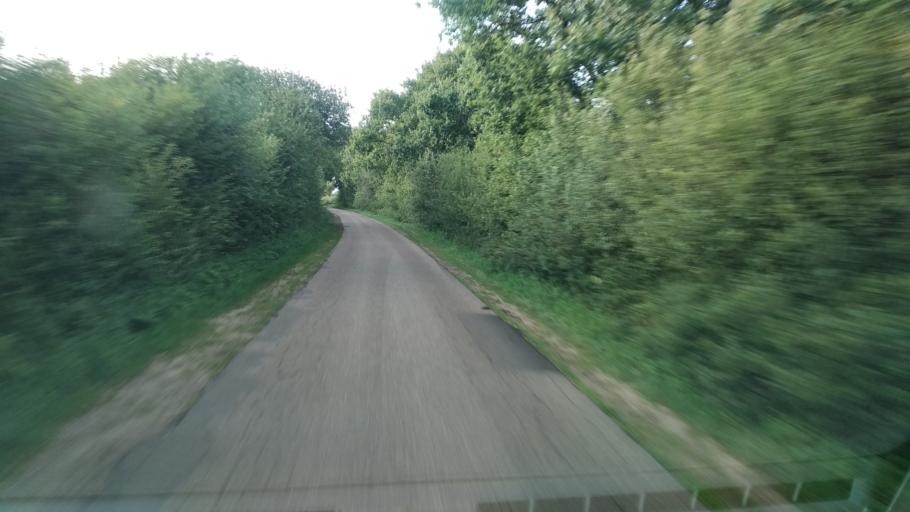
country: DE
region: Schleswig-Holstein
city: Klein Bennebek
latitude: 54.4081
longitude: 9.4596
